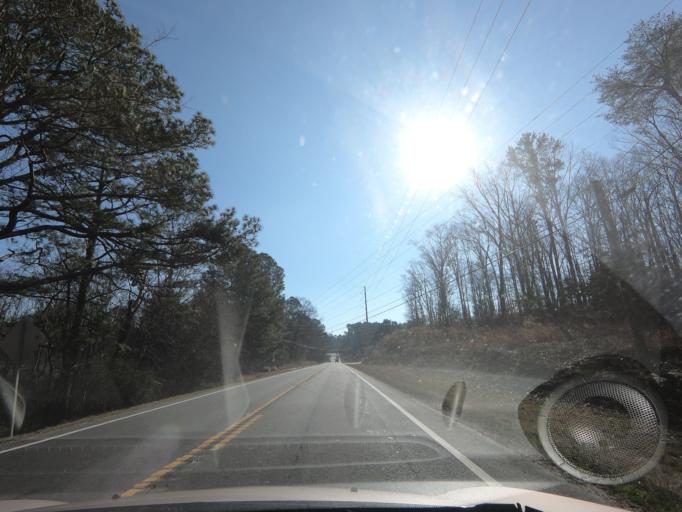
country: US
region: Georgia
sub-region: Forsyth County
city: Cumming
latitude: 34.3041
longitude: -84.2017
